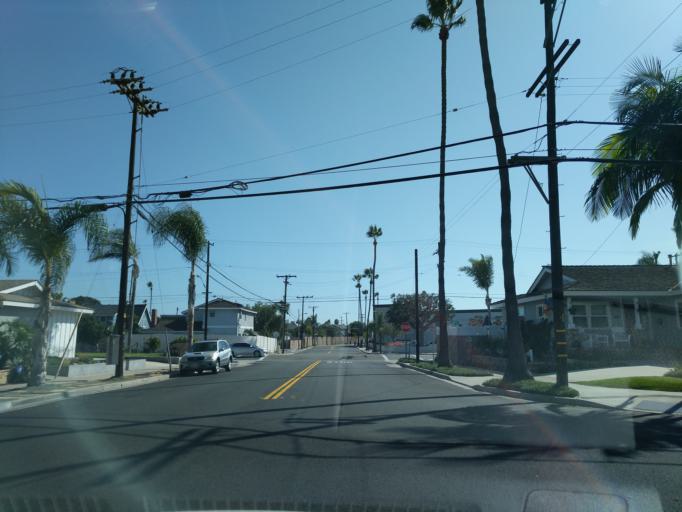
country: US
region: California
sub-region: Orange County
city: Seal Beach
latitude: 33.7455
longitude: -118.0994
